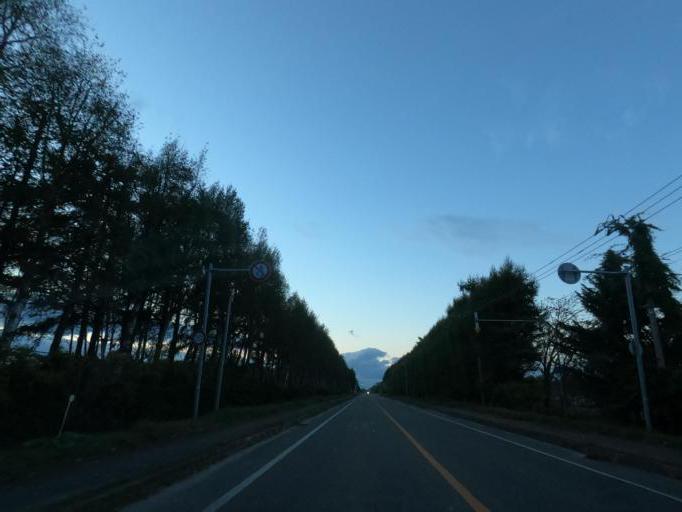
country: JP
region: Hokkaido
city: Obihiro
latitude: 42.6557
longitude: 143.1872
